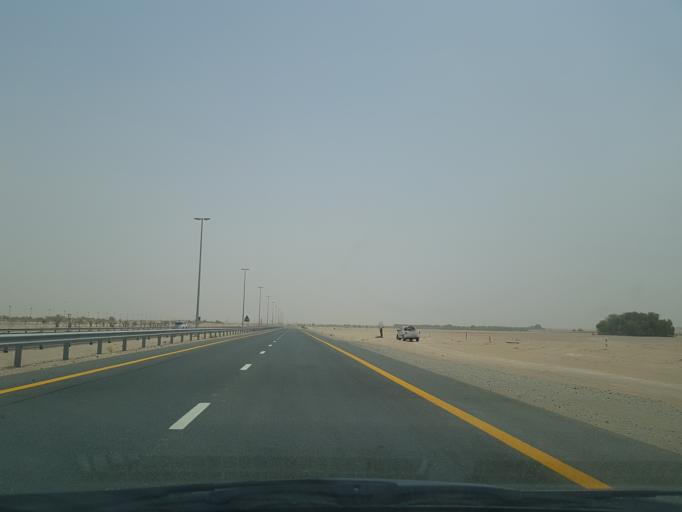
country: AE
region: Dubai
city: Dubai
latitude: 24.8724
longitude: 55.4158
